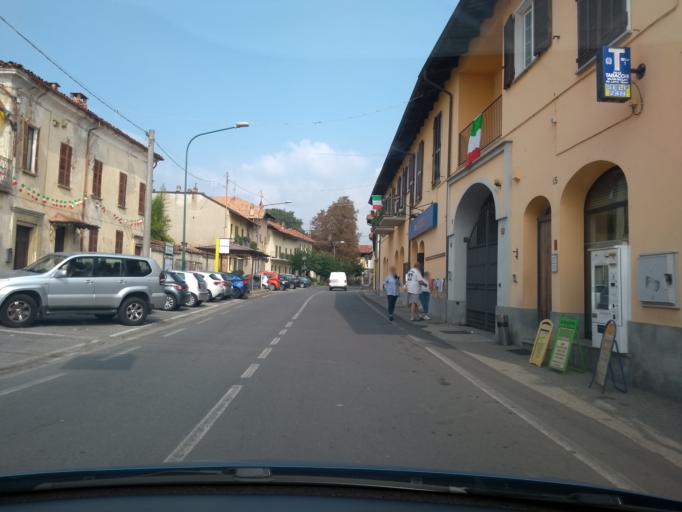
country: IT
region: Piedmont
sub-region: Provincia di Torino
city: Oglianico
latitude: 45.3417
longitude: 7.6919
